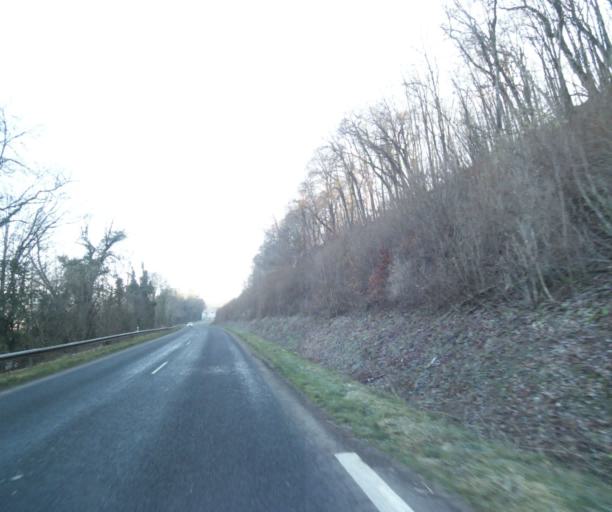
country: FR
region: Champagne-Ardenne
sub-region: Departement de la Haute-Marne
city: Bienville
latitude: 48.5532
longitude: 5.0679
